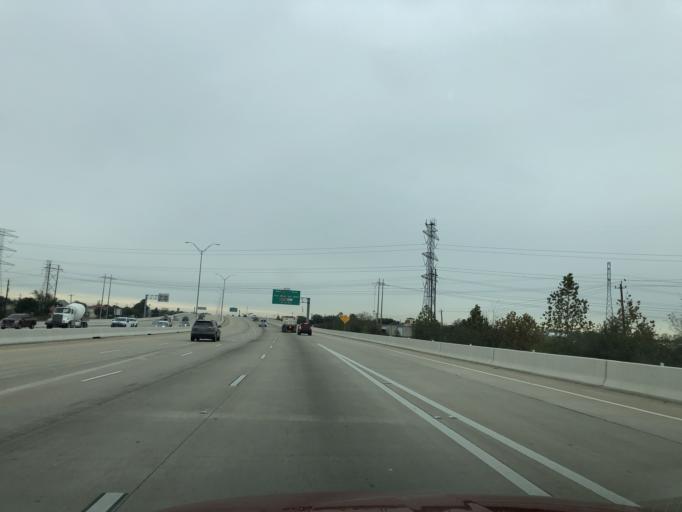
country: US
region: Texas
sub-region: Fort Bend County
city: Missouri City
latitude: 29.6226
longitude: -95.5133
